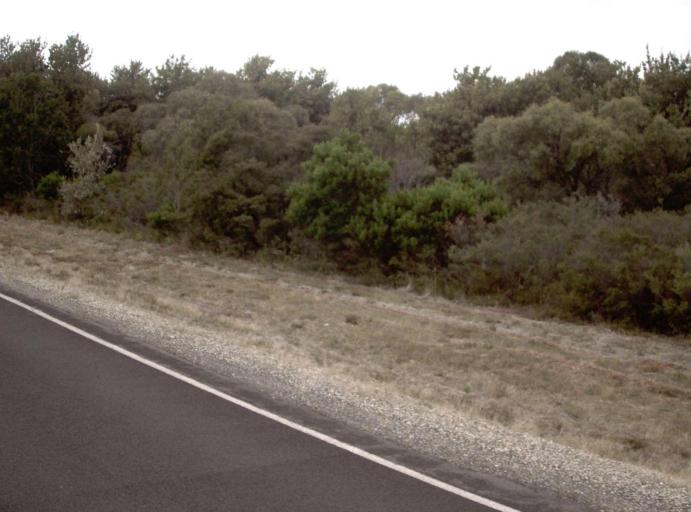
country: AU
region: Victoria
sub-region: East Gippsland
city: Bairnsdale
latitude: -38.1001
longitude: 147.5052
